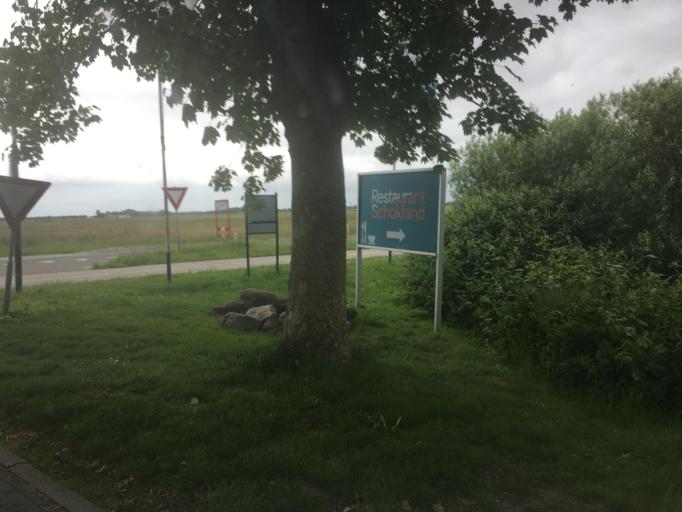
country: NL
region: Flevoland
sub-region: Gemeente Noordoostpolder
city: Ens
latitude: 52.6365
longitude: 5.7775
